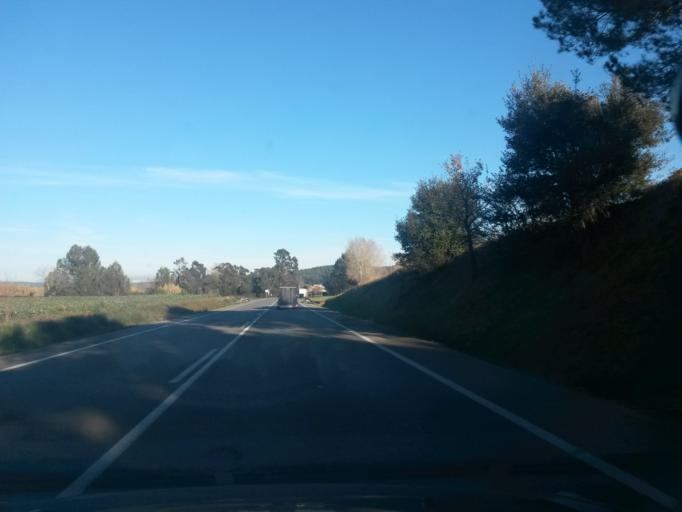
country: ES
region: Catalonia
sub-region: Provincia de Girona
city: Sant Joan de Mollet
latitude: 42.0433
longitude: 2.9460
